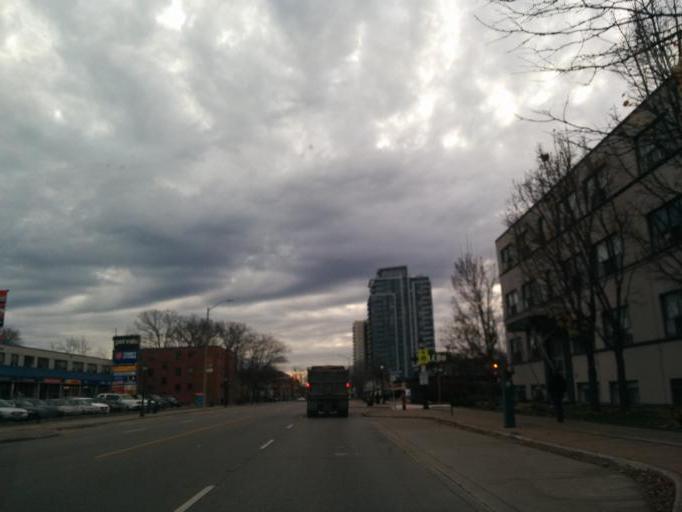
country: CA
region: Ontario
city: Mississauga
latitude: 43.5583
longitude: -79.5785
